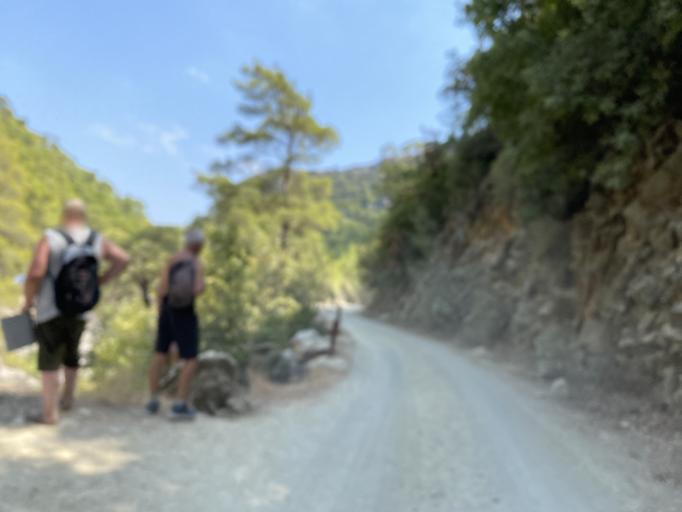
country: TR
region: Antalya
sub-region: Kemer
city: Goeynuek
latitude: 36.6808
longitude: 30.5226
